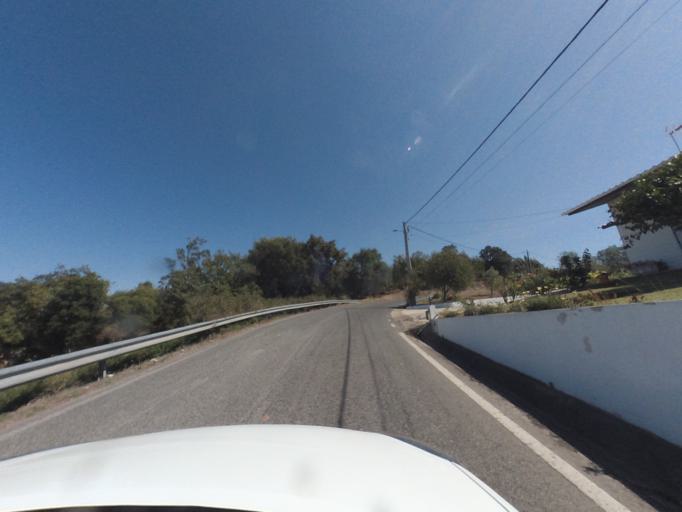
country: PT
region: Leiria
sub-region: Alcobaca
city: Turquel
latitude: 39.4847
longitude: -8.9891
